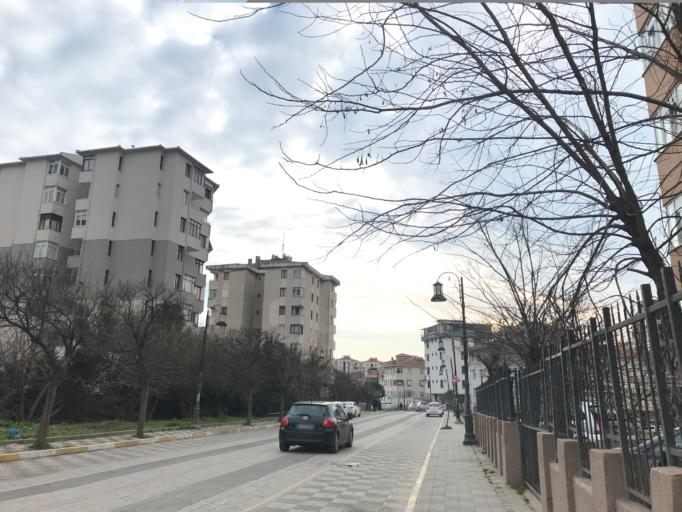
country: TR
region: Istanbul
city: Maltepe
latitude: 40.9312
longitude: 29.1309
